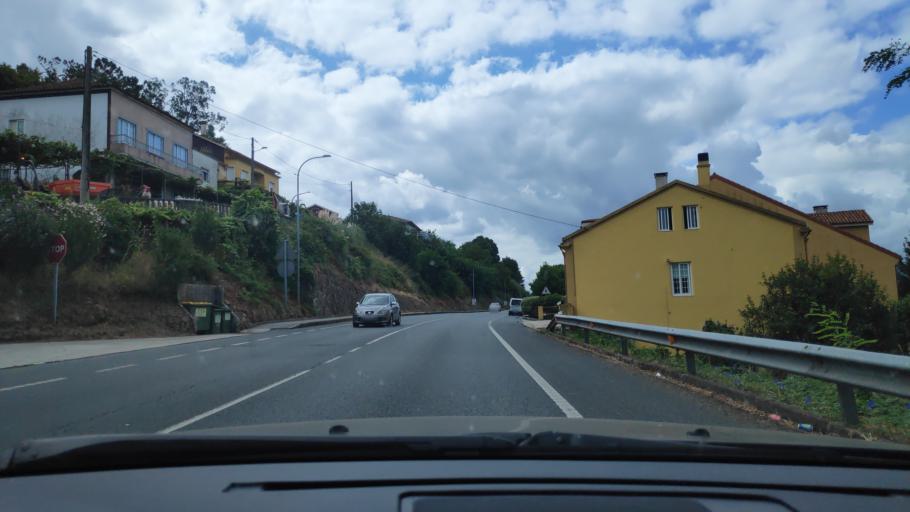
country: ES
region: Galicia
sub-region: Provincia da Coruna
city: Padron
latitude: 42.7241
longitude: -8.6508
